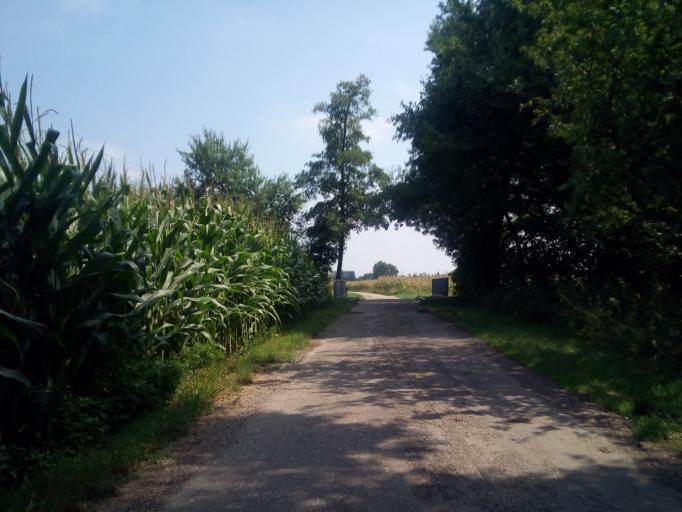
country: DE
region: Baden-Wuerttemberg
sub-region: Freiburg Region
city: Kehl
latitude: 48.6017
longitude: 7.8537
